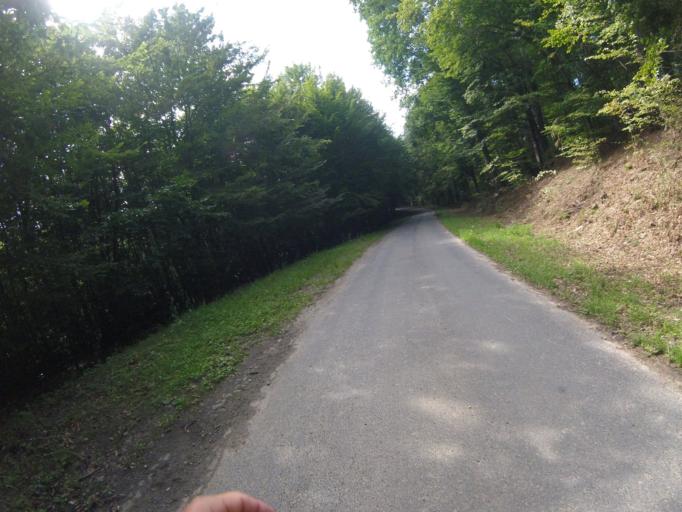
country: HR
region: Medimurska
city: Podturen
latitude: 46.5450
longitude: 16.6245
